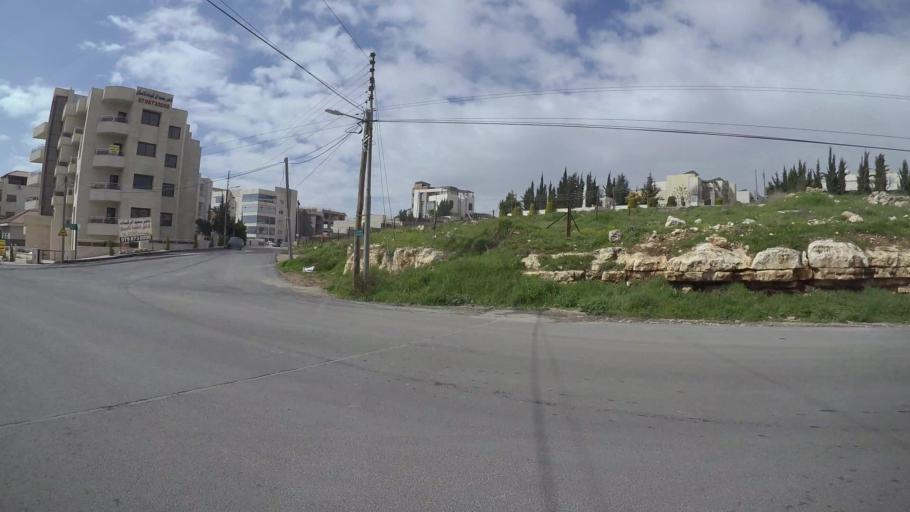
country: JO
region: Amman
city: Al Jubayhah
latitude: 31.9980
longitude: 35.8359
